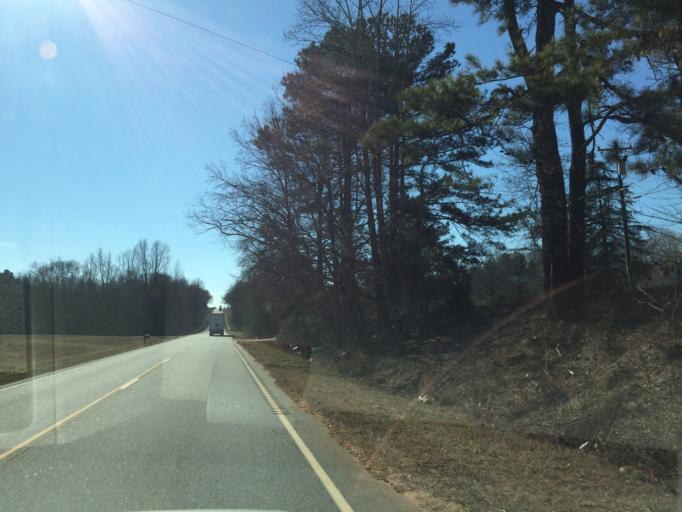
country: US
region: South Carolina
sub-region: Anderson County
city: Williamston
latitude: 34.6609
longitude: -82.5174
